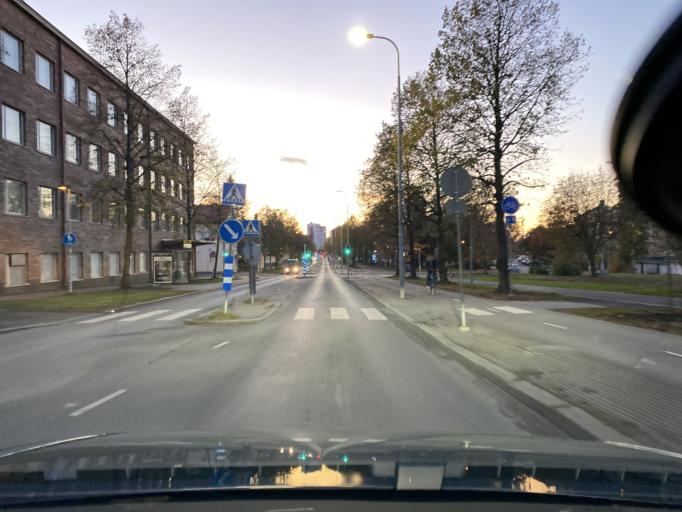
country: FI
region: Pirkanmaa
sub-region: Tampere
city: Tampere
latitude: 61.4706
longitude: 23.7350
